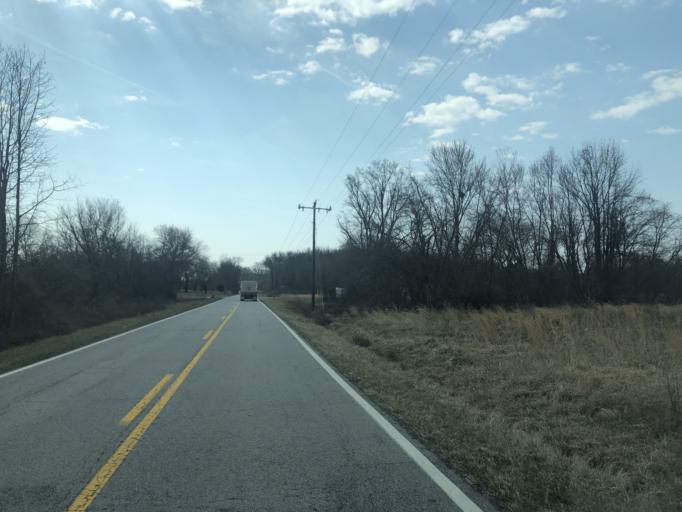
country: US
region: Maryland
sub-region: Queen Anne's County
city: Centreville
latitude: 39.0789
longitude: -75.9337
